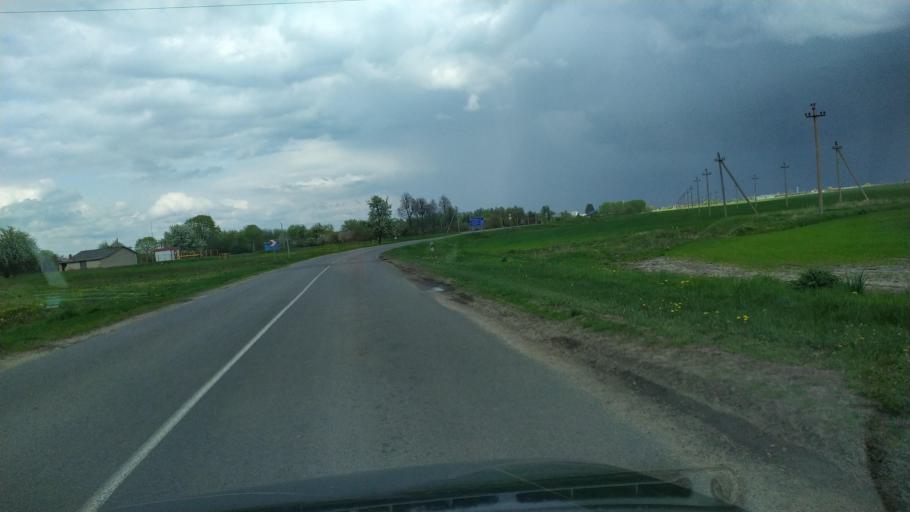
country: BY
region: Brest
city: Pruzhany
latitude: 52.6512
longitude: 24.3815
